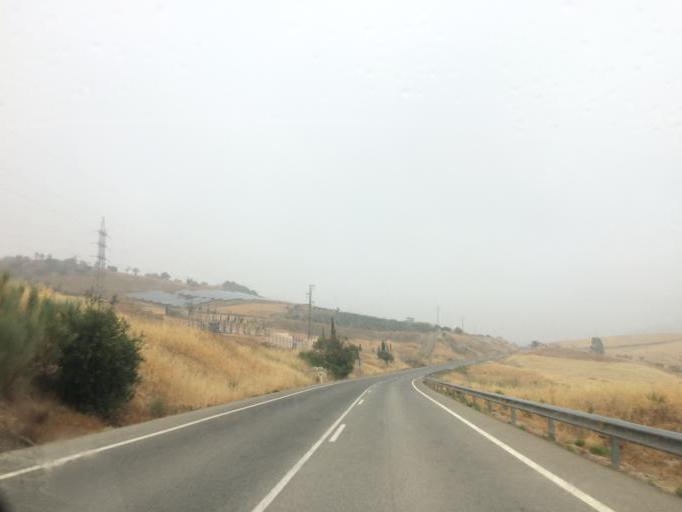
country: ES
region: Andalusia
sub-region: Provincia de Malaga
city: Casabermeja
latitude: 36.9005
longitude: -4.4240
